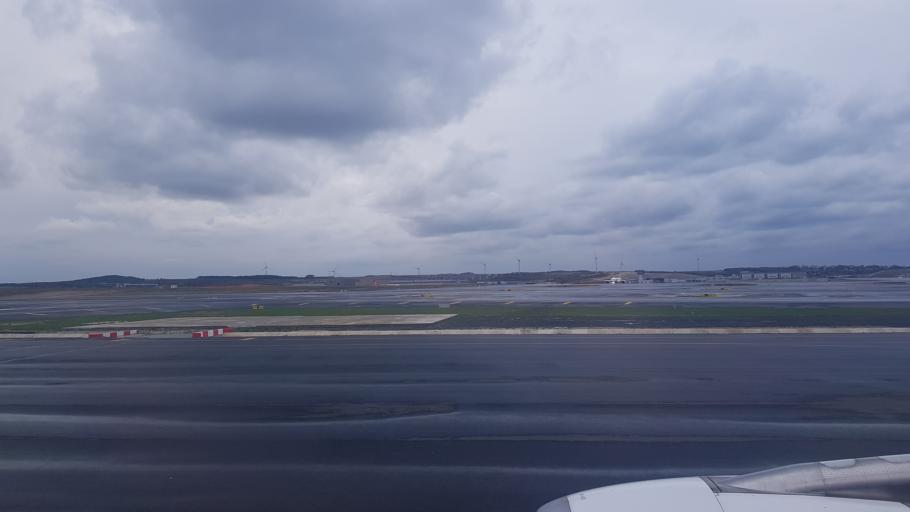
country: TR
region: Istanbul
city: Durusu
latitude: 41.2637
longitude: 28.7346
